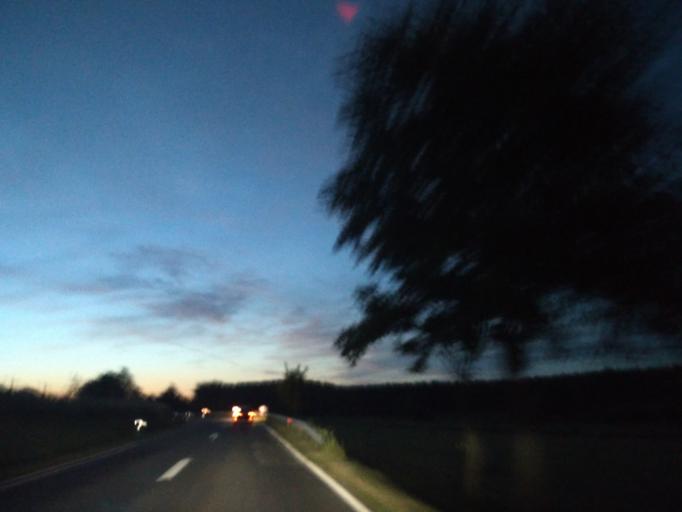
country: HU
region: Vas
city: Vasvar
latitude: 46.9749
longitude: 16.8430
